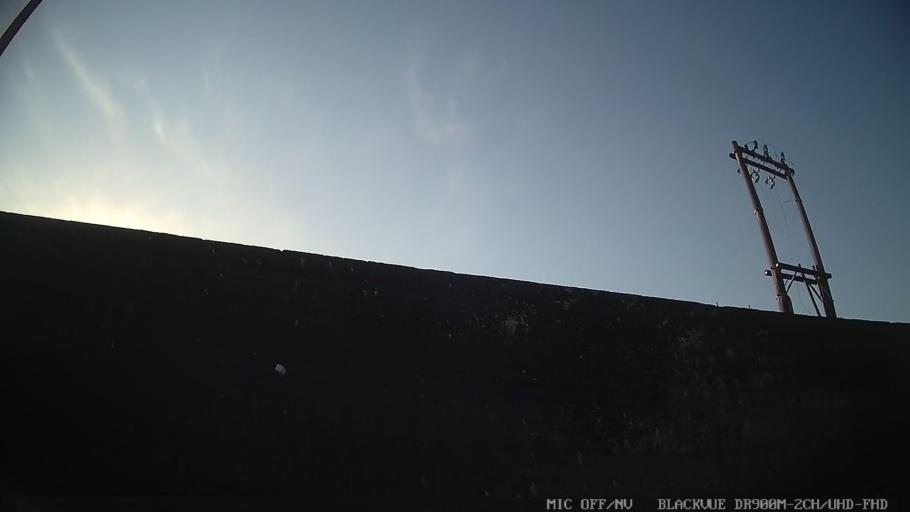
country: BR
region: Sao Paulo
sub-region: Guaruja
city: Guaruja
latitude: -23.9719
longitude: -46.2634
